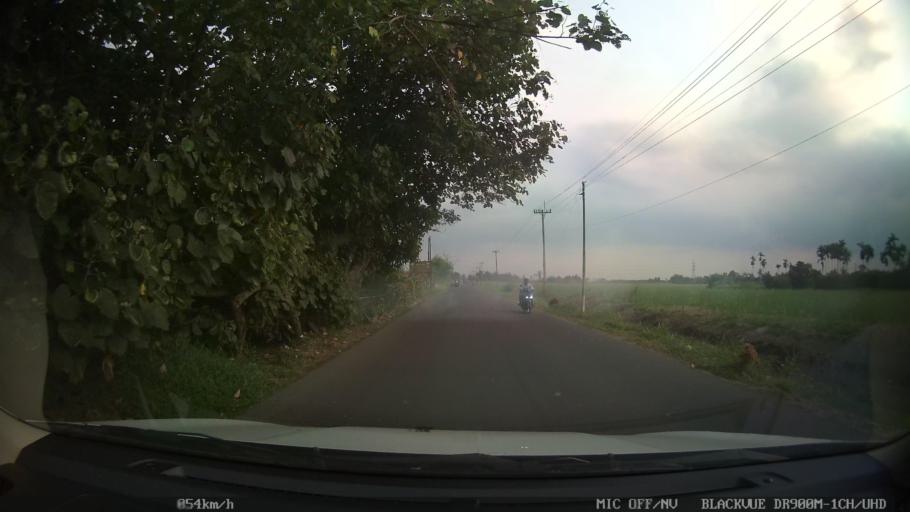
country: ID
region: North Sumatra
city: Sunggal
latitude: 3.5889
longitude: 98.5518
